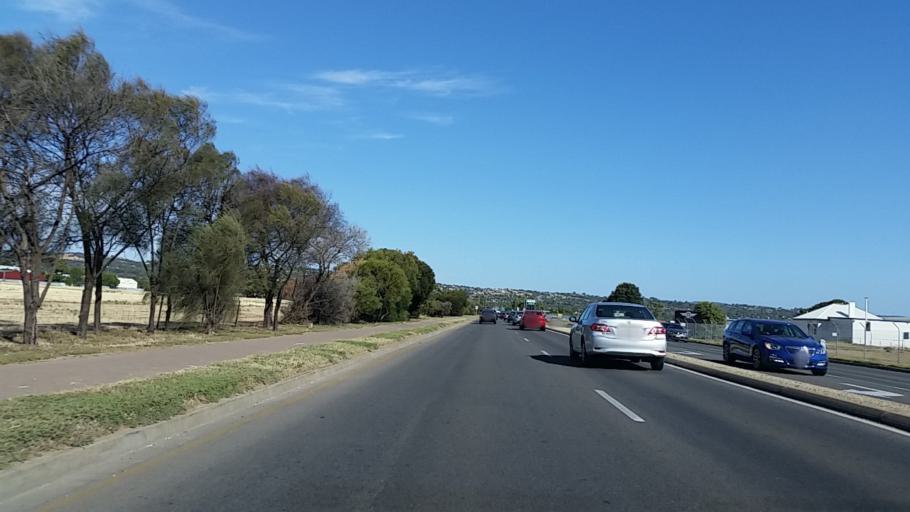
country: AU
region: South Australia
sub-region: Salisbury
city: Salisbury
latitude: -34.7875
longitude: 138.6402
